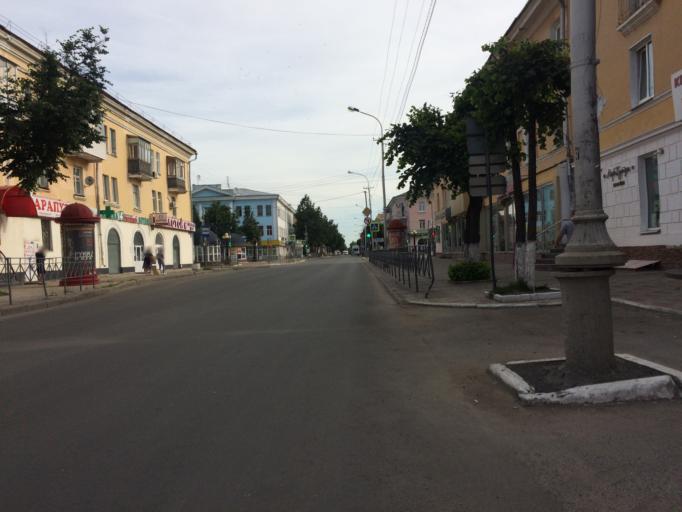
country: RU
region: Mariy-El
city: Yoshkar-Ola
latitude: 56.6341
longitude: 47.8969
